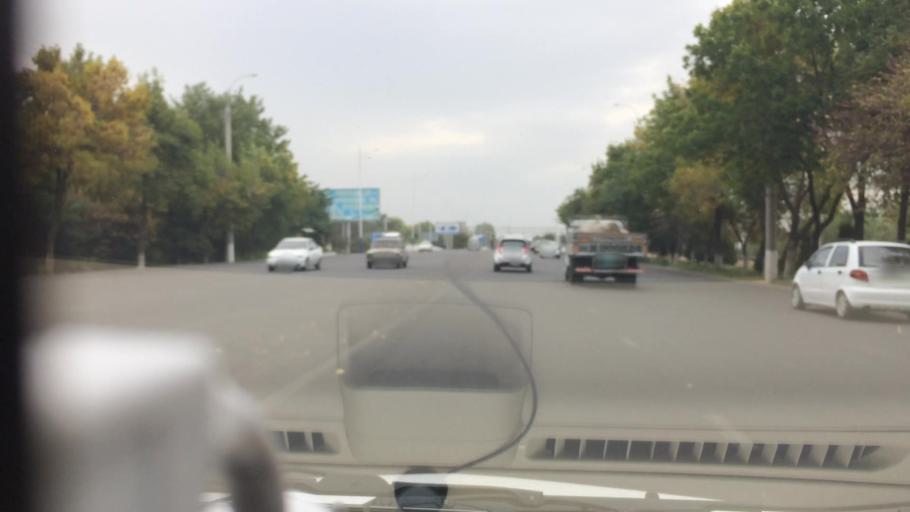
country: UZ
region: Toshkent Shahri
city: Tashkent
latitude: 41.3063
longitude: 69.2999
